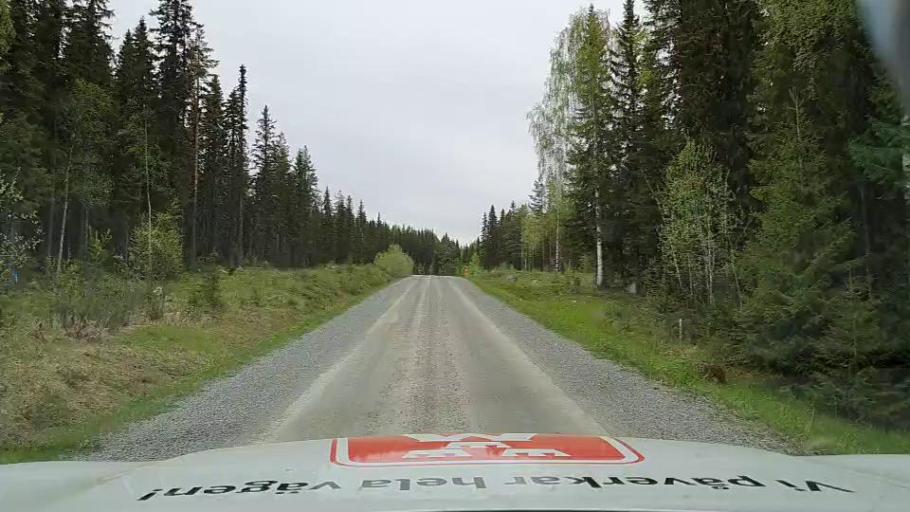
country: SE
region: Jaemtland
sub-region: OEstersunds Kommun
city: Brunflo
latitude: 62.6500
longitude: 14.9256
